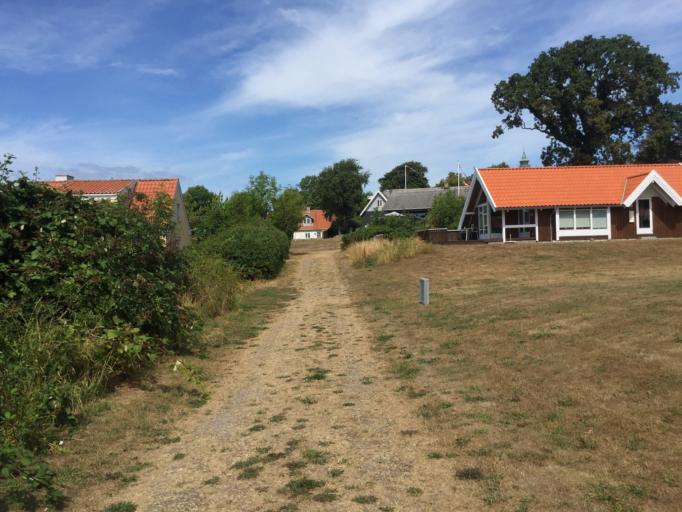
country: DK
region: Central Jutland
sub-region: Samso Kommune
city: Tranebjerg
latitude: 55.9476
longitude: 10.4439
